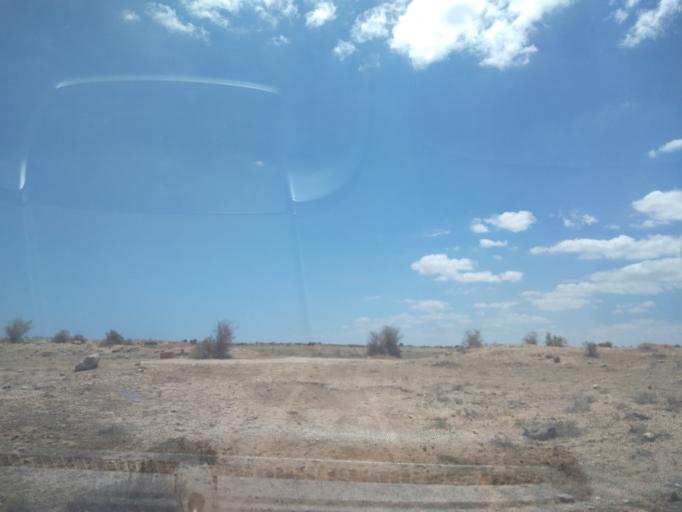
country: TN
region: Susah
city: Harqalah
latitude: 36.1720
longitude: 10.4404
